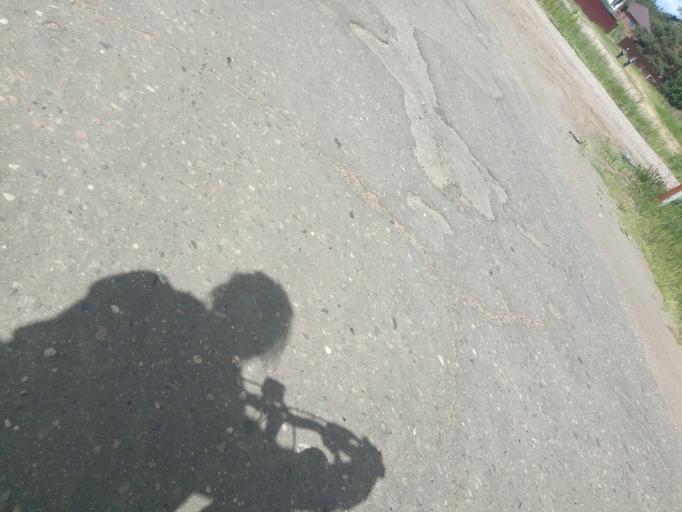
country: RU
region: Jaroslavl
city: Yaroslavl
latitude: 57.6511
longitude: 39.9930
